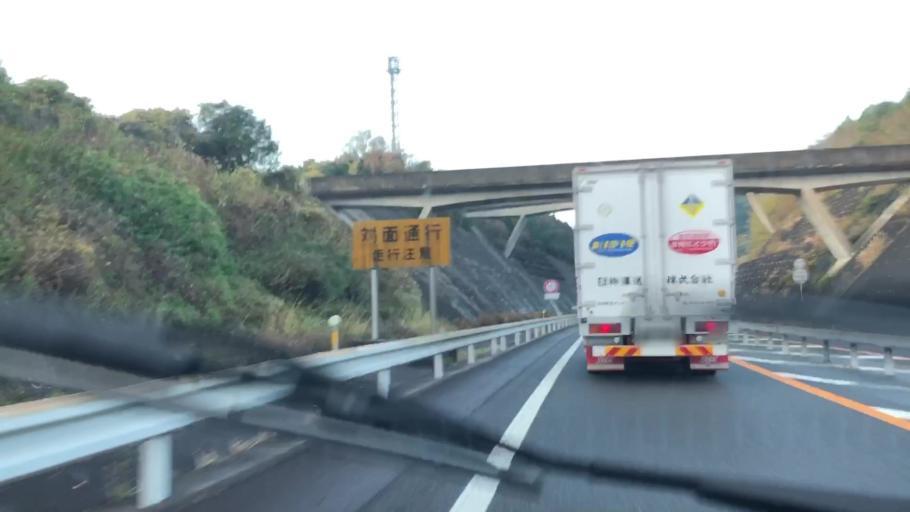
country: JP
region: Nagasaki
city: Sasebo
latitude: 33.1518
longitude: 129.8098
